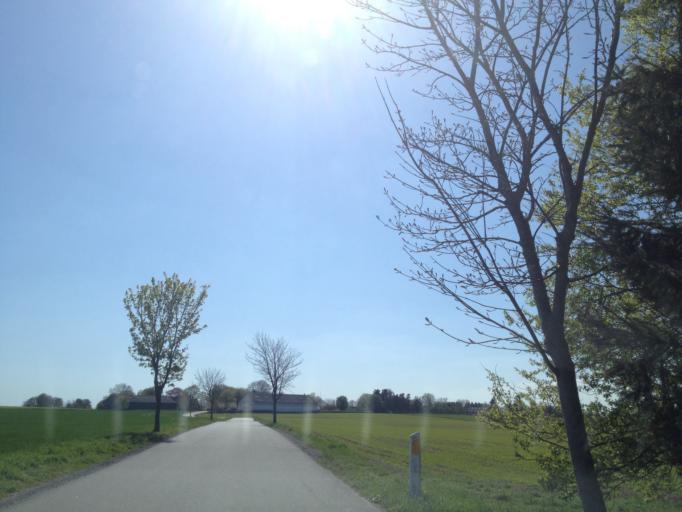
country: DK
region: Zealand
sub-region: Roskilde Kommune
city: Viby
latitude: 55.5164
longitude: 12.0126
